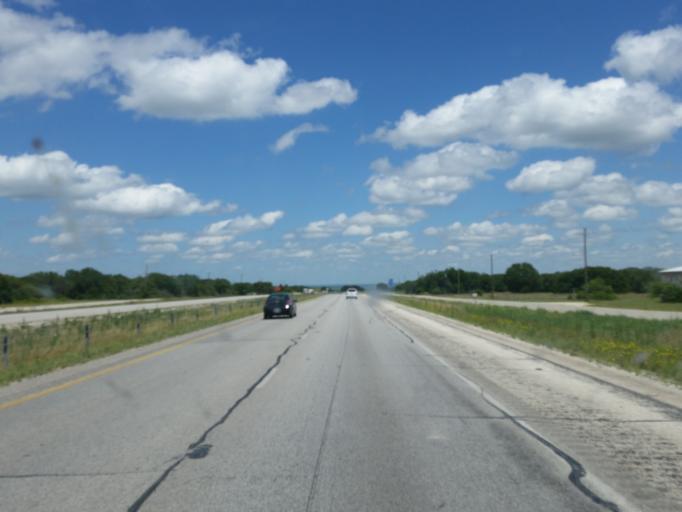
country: US
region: Texas
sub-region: Callahan County
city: Clyde
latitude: 32.4065
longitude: -99.4463
